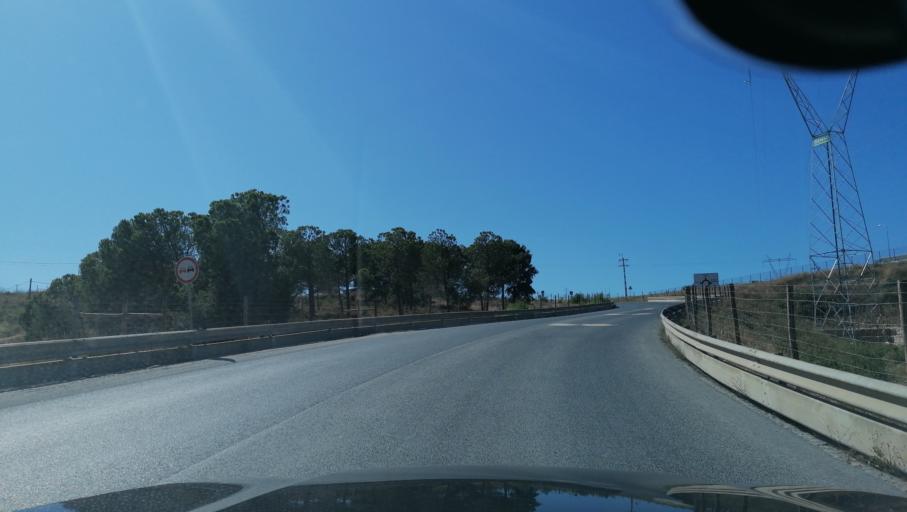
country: PT
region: Lisbon
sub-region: Alenquer
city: Alenquer
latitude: 39.0663
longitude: -9.0034
